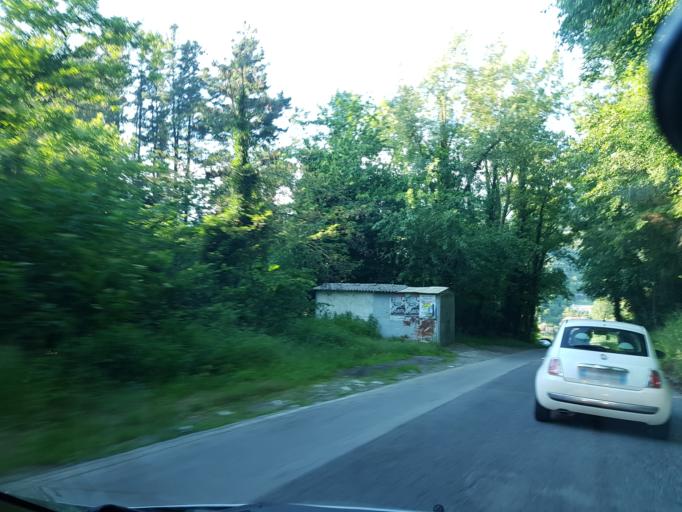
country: IT
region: Tuscany
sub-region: Provincia di Massa-Carrara
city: Casola in Lunigiana
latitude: 44.1904
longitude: 10.1940
